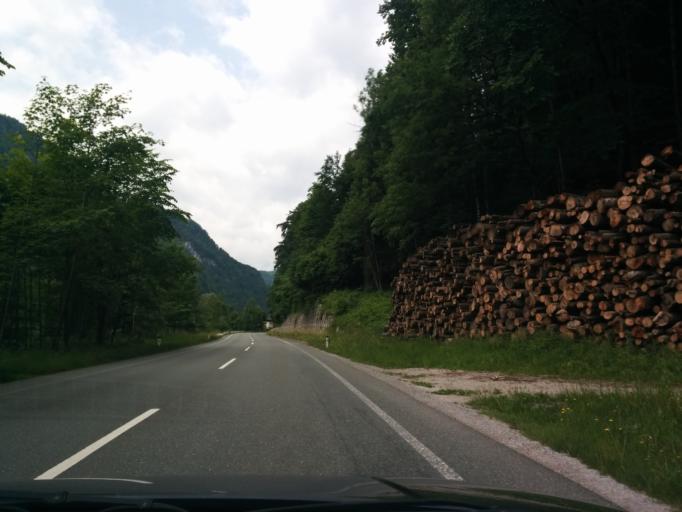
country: AT
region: Salzburg
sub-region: Politischer Bezirk Hallein
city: Scheffau am Tennengebirge
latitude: 47.5797
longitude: 13.2597
